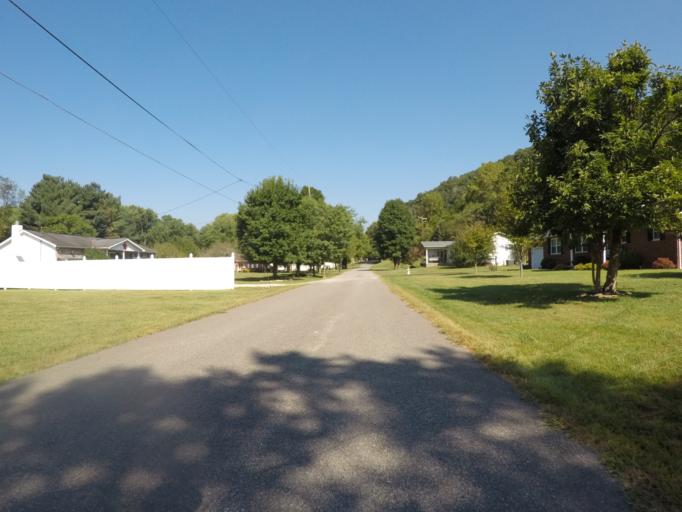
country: US
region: West Virginia
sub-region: Cabell County
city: Barboursville
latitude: 38.3777
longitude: -82.2812
